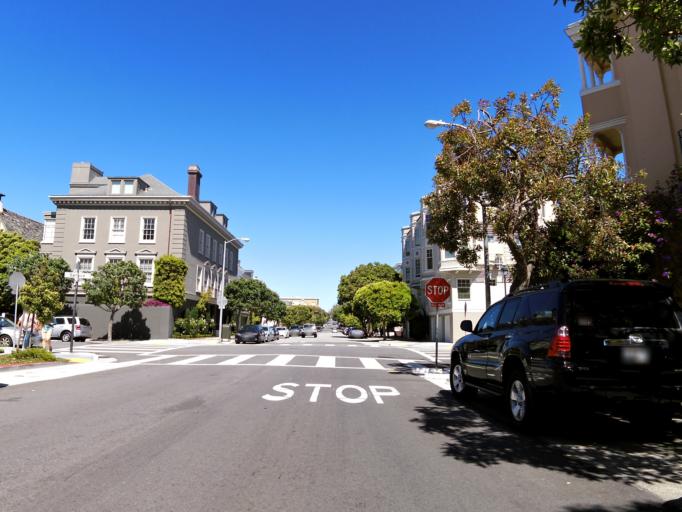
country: US
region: California
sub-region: San Francisco County
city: San Francisco
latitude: 37.7882
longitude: -122.4541
